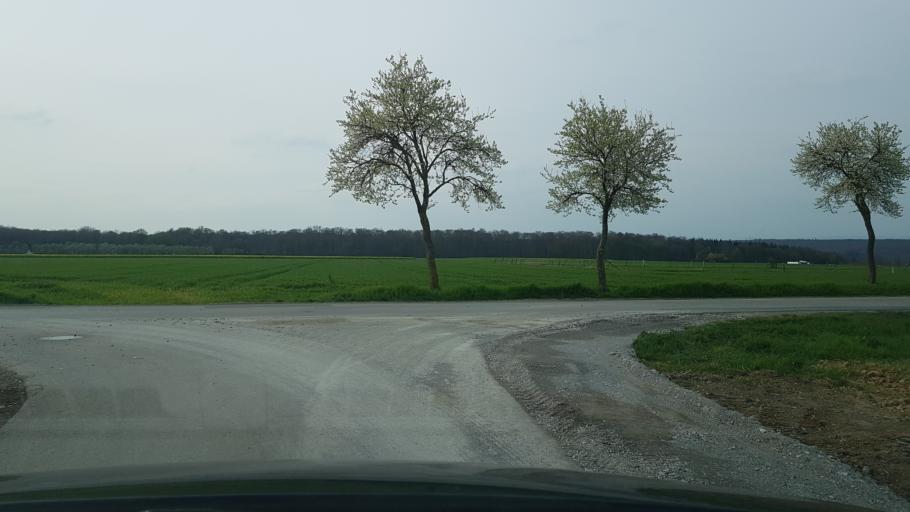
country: DE
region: North Rhine-Westphalia
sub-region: Regierungsbezirk Detmold
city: Paderborn
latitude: 51.6241
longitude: 8.7352
